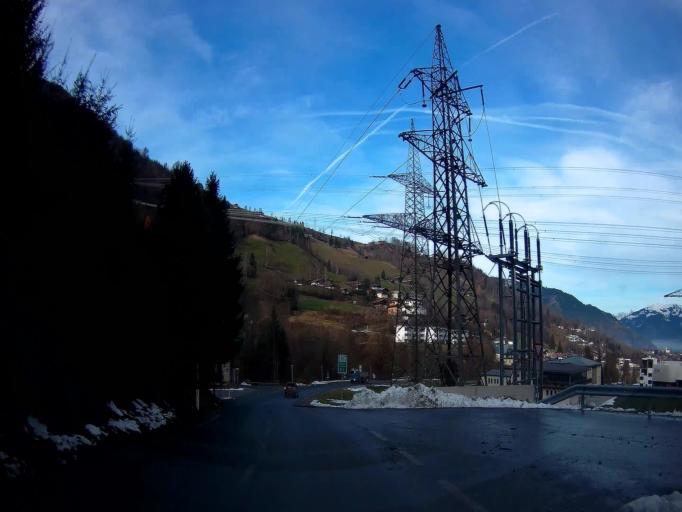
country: AT
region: Salzburg
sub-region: Politischer Bezirk Zell am See
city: Kaprun
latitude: 47.2586
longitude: 12.7407
